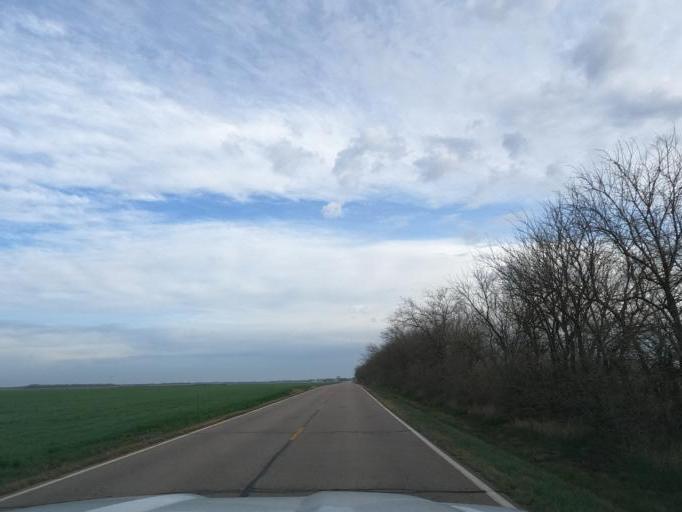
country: US
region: Kansas
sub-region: Reno County
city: Nickerson
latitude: 37.9890
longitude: -98.1786
